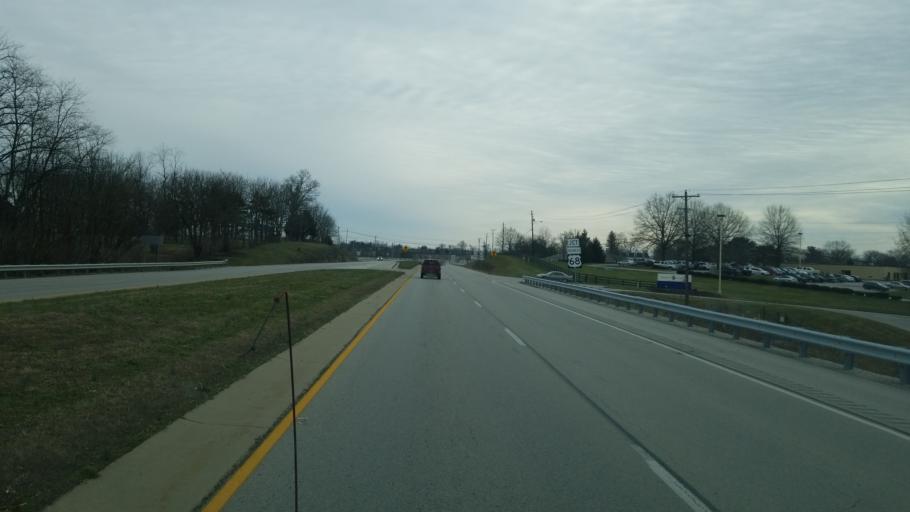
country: US
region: Kentucky
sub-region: Bourbon County
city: Paris
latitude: 38.2231
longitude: -84.2390
